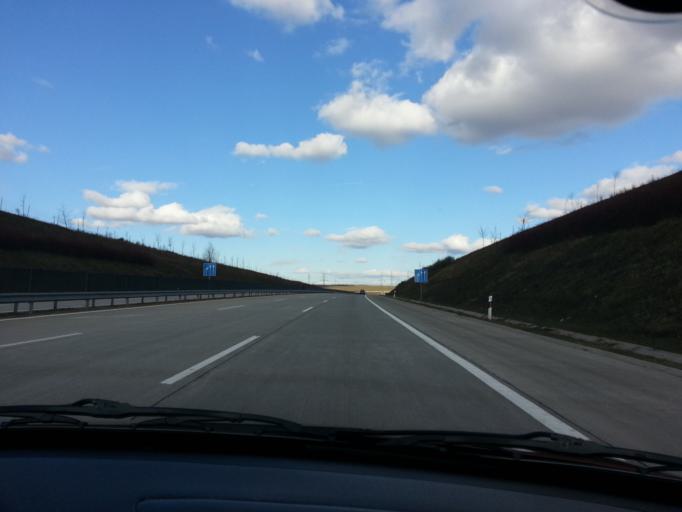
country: HU
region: Pest
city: Nagytarcsa
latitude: 47.5364
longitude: 19.3058
